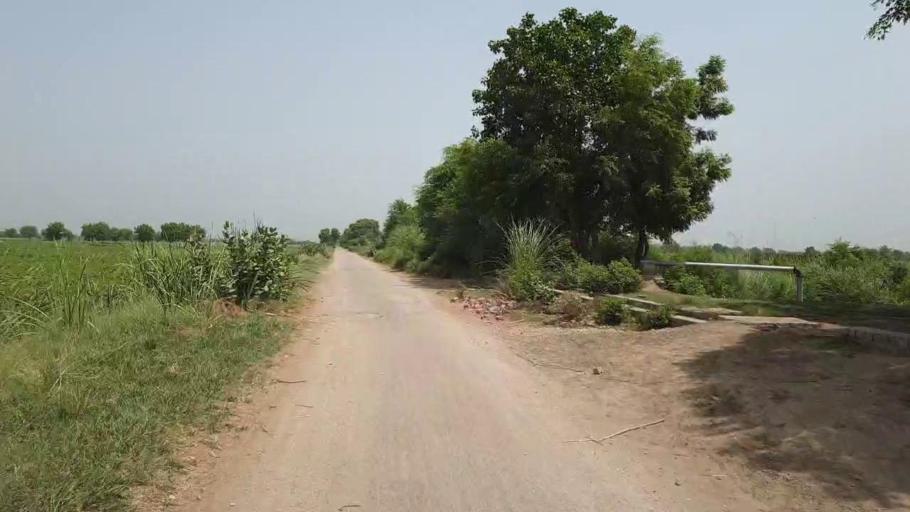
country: PK
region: Sindh
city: Nawabshah
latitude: 26.2882
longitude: 68.3094
